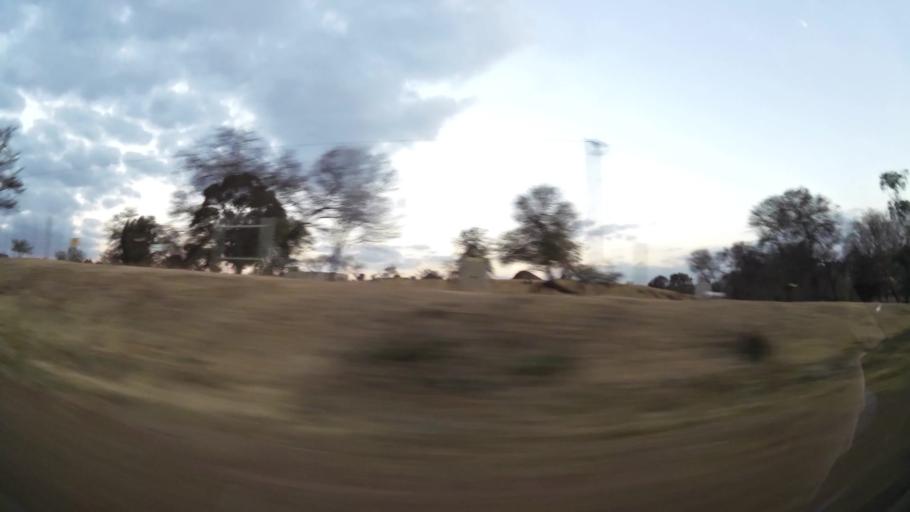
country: ZA
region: Gauteng
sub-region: West Rand District Municipality
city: Krugersdorp
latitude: -26.0631
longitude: 27.6964
